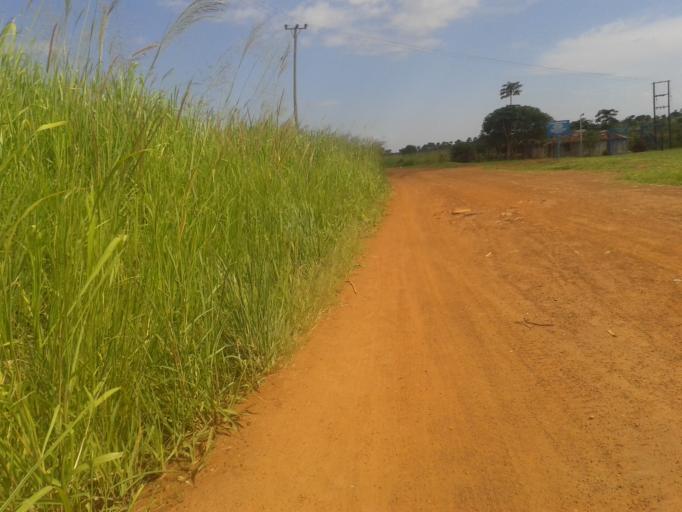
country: UG
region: Northern Region
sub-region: Gulu District
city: Gulu
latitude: 2.8211
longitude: 32.2680
